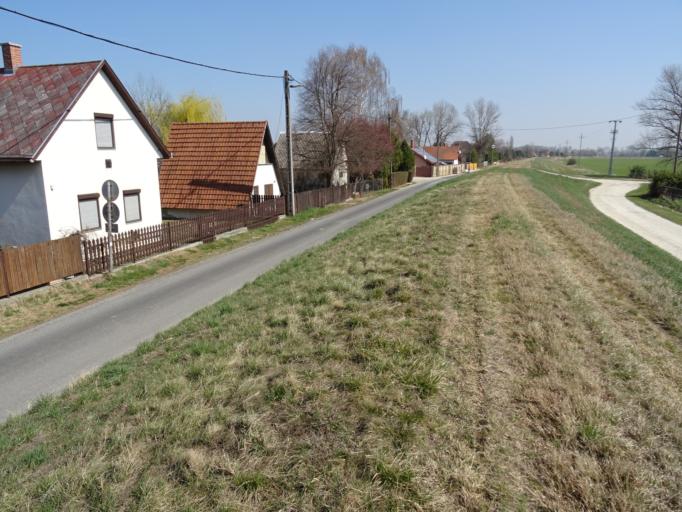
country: HU
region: Pest
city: Domsod
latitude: 47.1092
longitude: 18.9861
